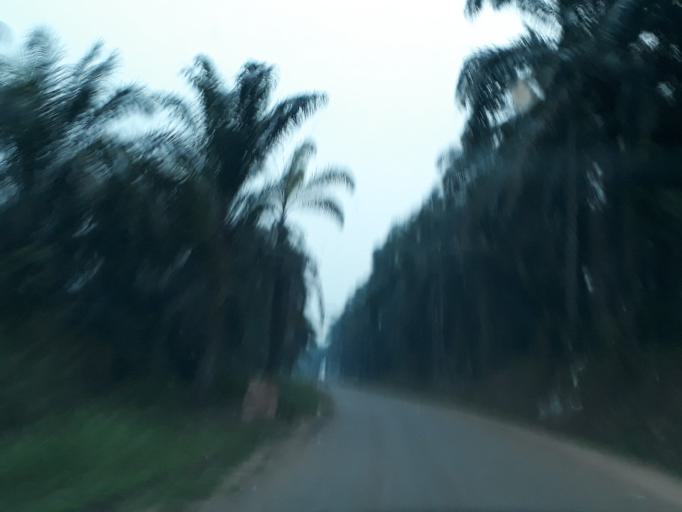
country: CD
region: Bandundu
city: Kikwit
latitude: -5.0718
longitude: 18.8760
